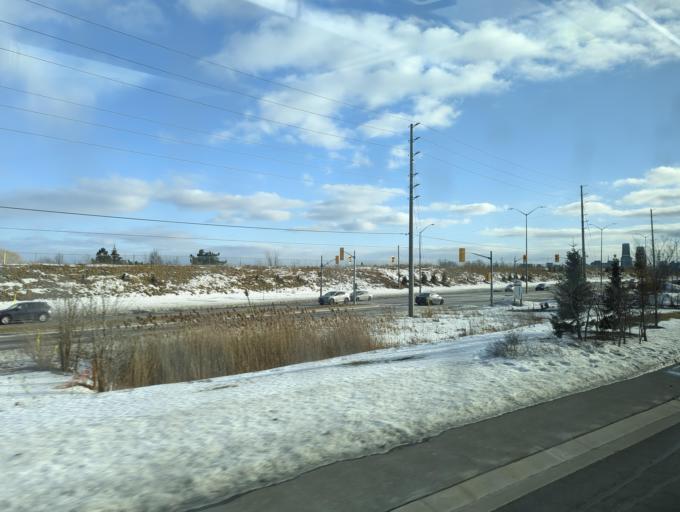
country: CA
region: Ontario
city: Mississauga
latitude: 43.6192
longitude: -79.6260
